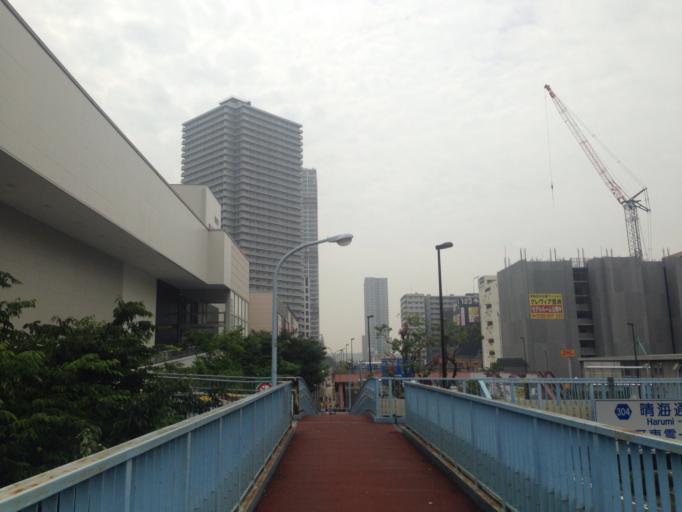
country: JP
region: Tokyo
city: Urayasu
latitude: 35.6492
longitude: 139.8016
